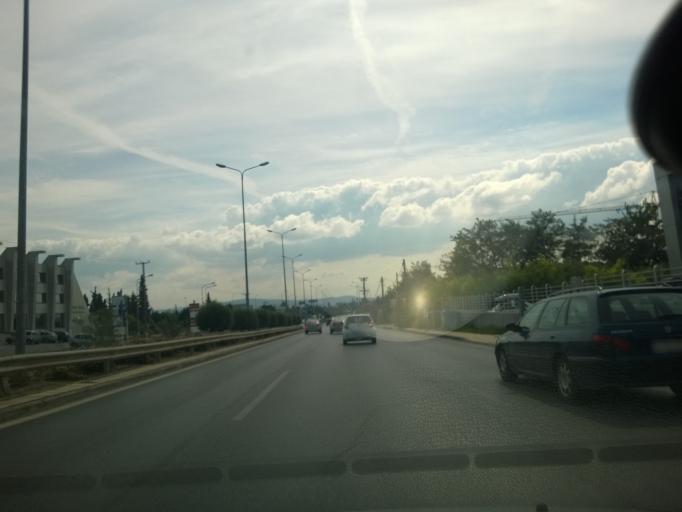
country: GR
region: Central Macedonia
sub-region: Nomos Thessalonikis
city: Kalamaria
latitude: 40.5564
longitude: 22.9788
